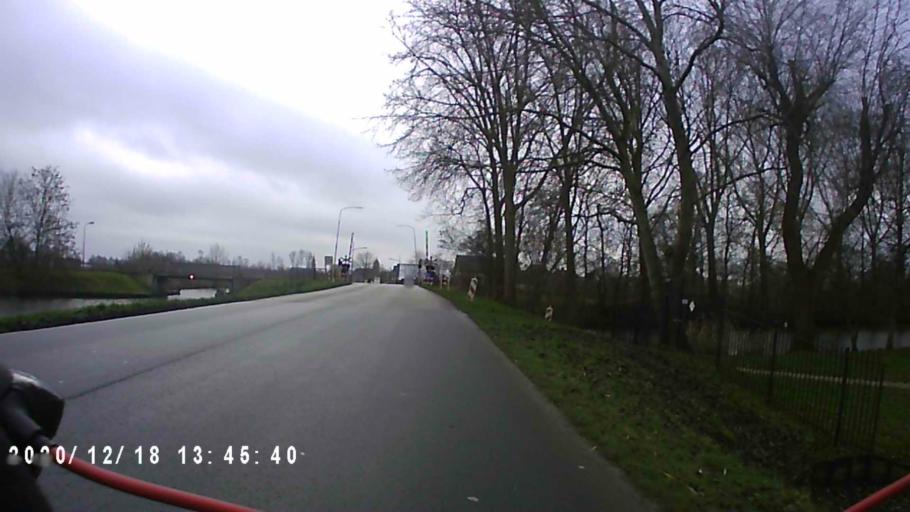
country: NL
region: Groningen
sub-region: Gemeente Bedum
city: Bedum
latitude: 53.3093
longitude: 6.6001
